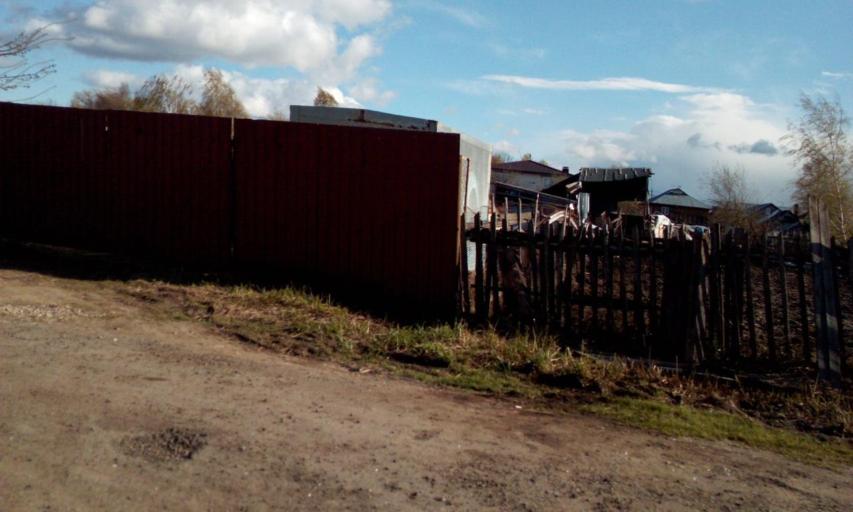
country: RU
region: Moskovskaya
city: Zhavoronki
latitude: 55.6548
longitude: 37.1502
